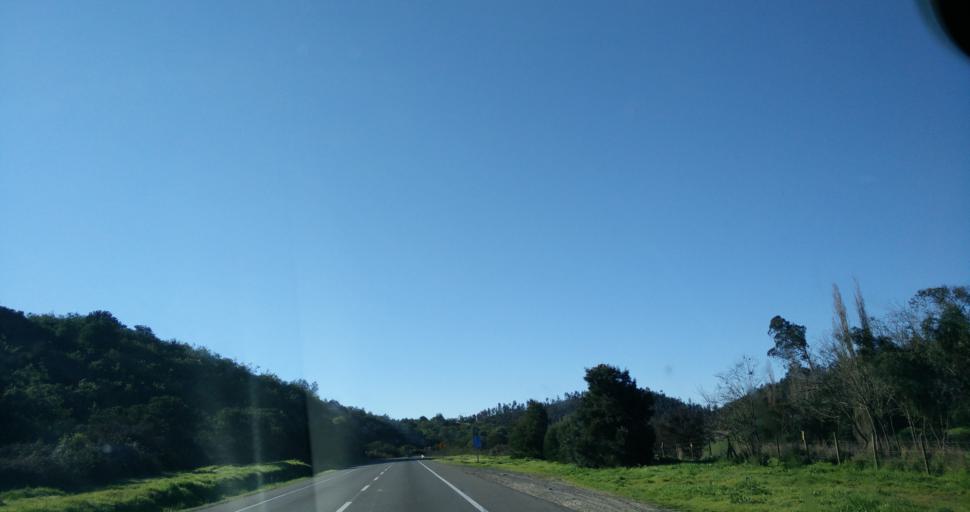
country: CL
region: Valparaiso
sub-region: San Antonio Province
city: Cartagena
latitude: -33.4235
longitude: -71.4484
